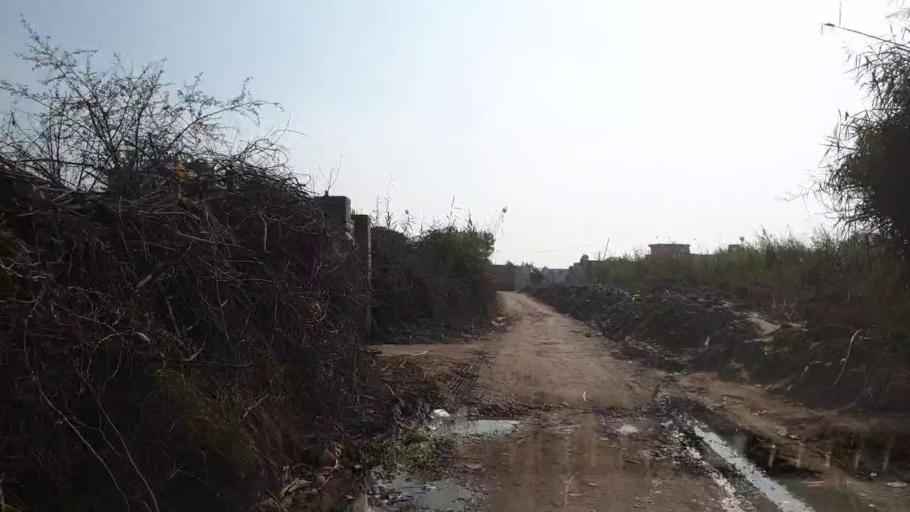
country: PK
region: Sindh
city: Tando Adam
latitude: 25.6590
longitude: 68.5766
